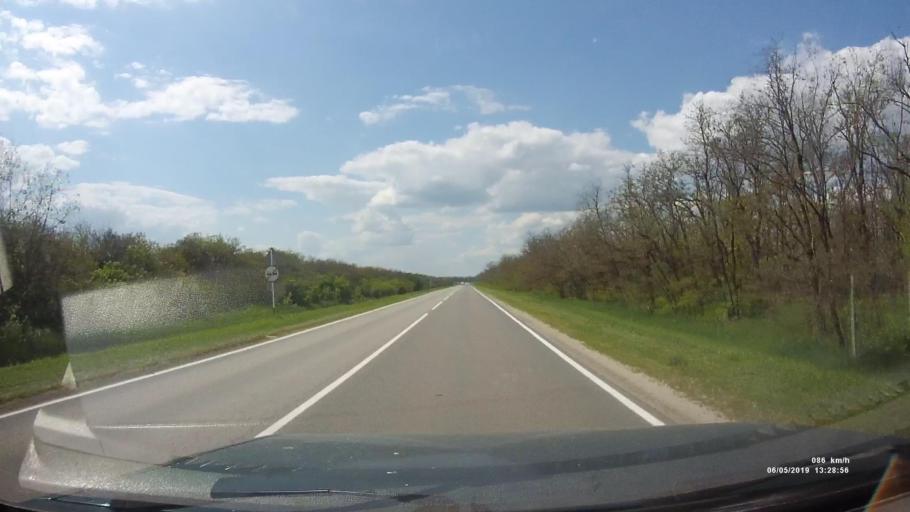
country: RU
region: Rostov
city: Ust'-Donetskiy
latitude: 47.6693
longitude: 40.8534
